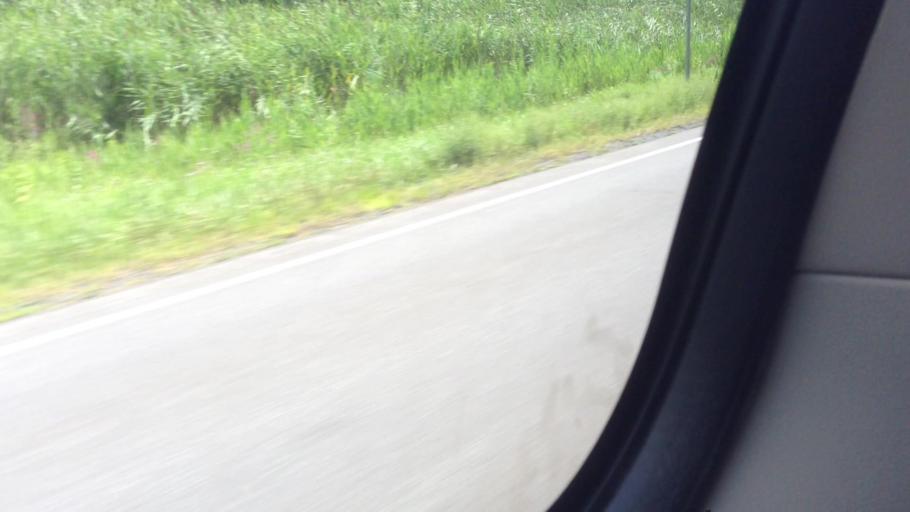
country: US
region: New York
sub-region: Dutchess County
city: Red Hook
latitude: 42.0146
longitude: -73.9062
